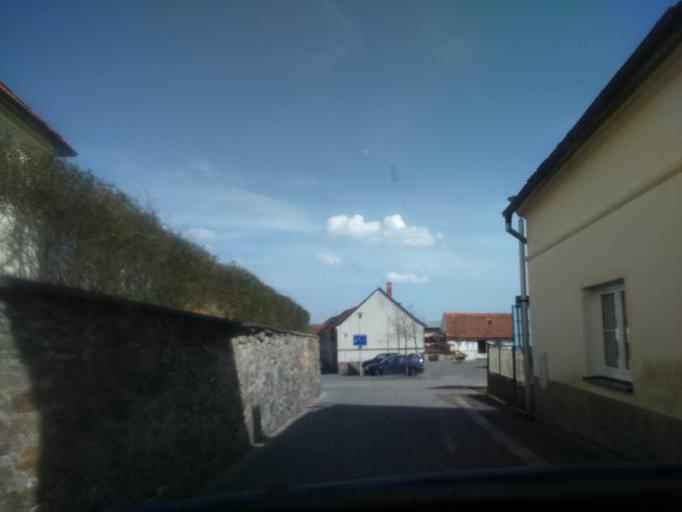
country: CZ
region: Plzensky
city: Cernosin
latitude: 49.8161
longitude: 12.8831
